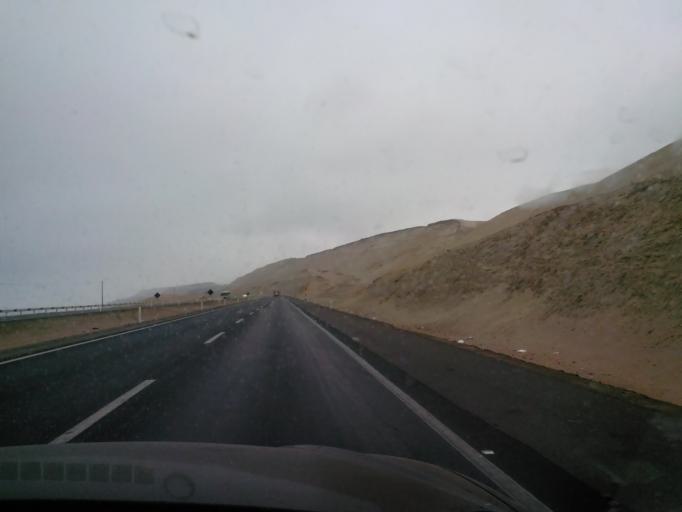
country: PE
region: Ica
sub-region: Provincia de Chincha
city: San Pedro
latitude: -13.3136
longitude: -76.2479
